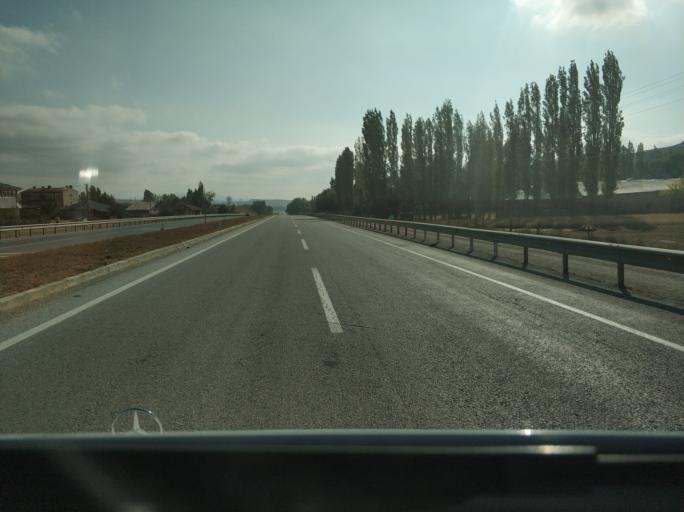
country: TR
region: Sivas
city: Yildizeli
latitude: 39.8429
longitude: 36.4727
